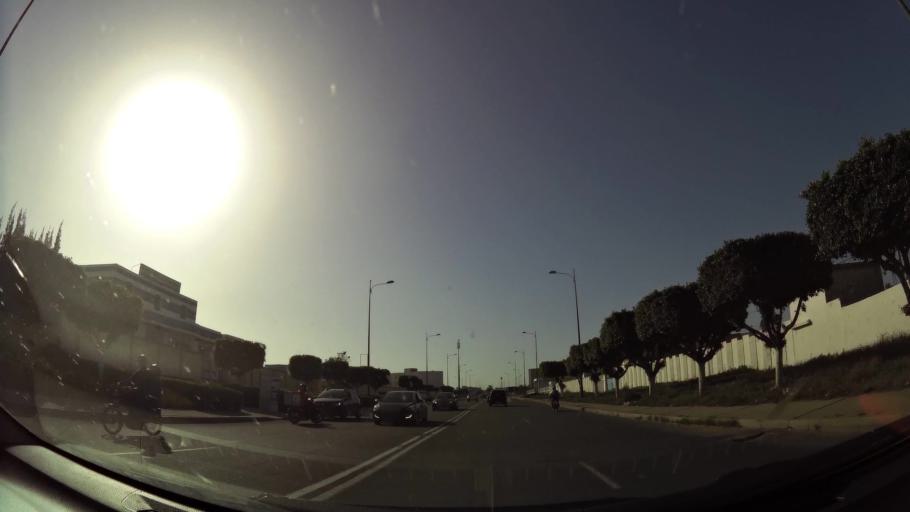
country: MA
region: Souss-Massa-Draa
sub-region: Inezgane-Ait Mellou
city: Inezgane
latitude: 30.3885
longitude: -9.5272
